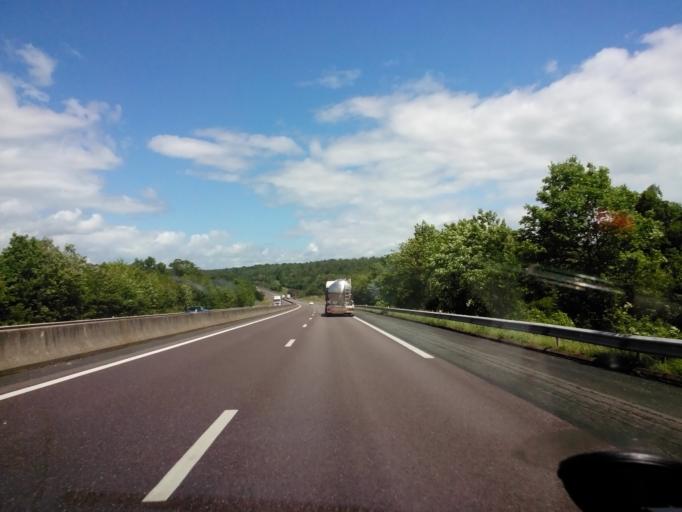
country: FR
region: Lorraine
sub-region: Departement de Meurthe-et-Moselle
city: Colombey-les-Belles
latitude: 48.4804
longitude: 5.8943
